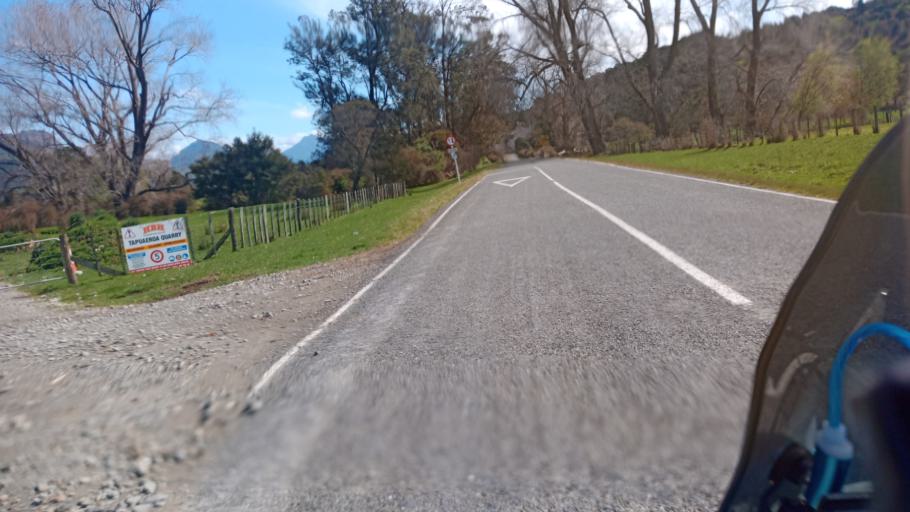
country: NZ
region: Gisborne
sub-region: Gisborne District
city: Gisborne
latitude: -37.8644
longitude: 178.2530
